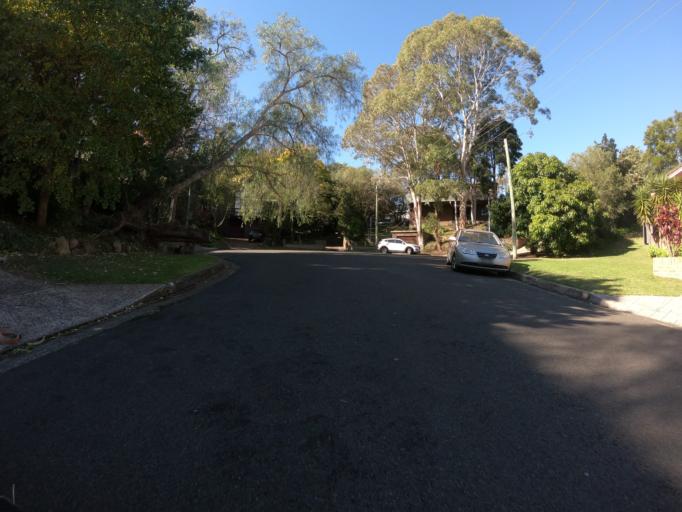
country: AU
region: New South Wales
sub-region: Wollongong
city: Mount Keira
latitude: -34.4159
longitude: 150.8555
